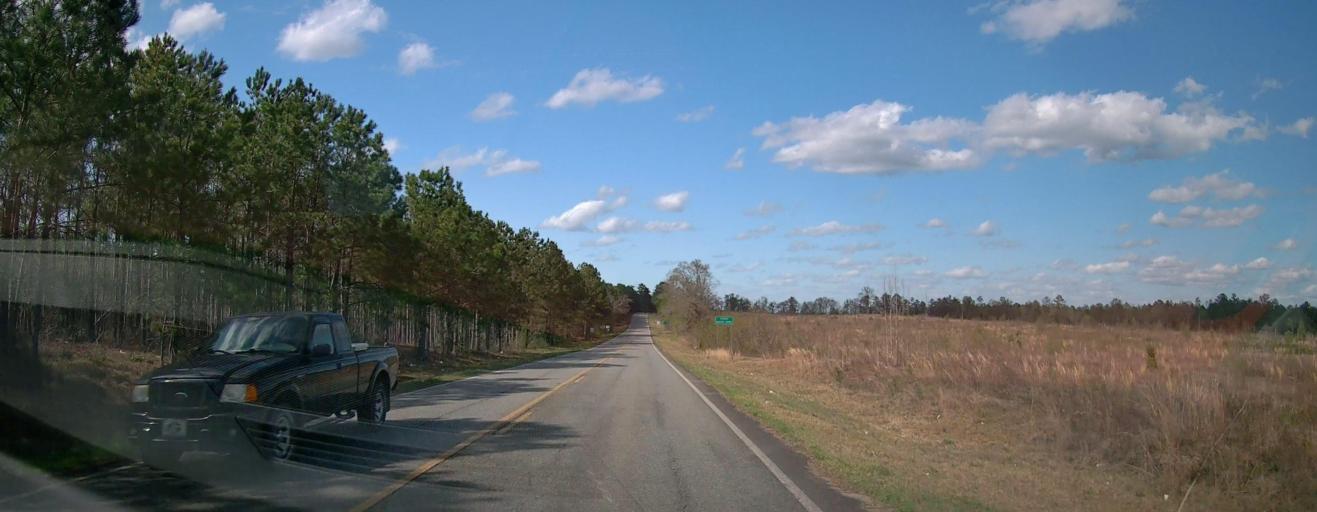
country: US
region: Georgia
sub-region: Wilkinson County
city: Gordon
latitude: 32.9491
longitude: -83.2905
